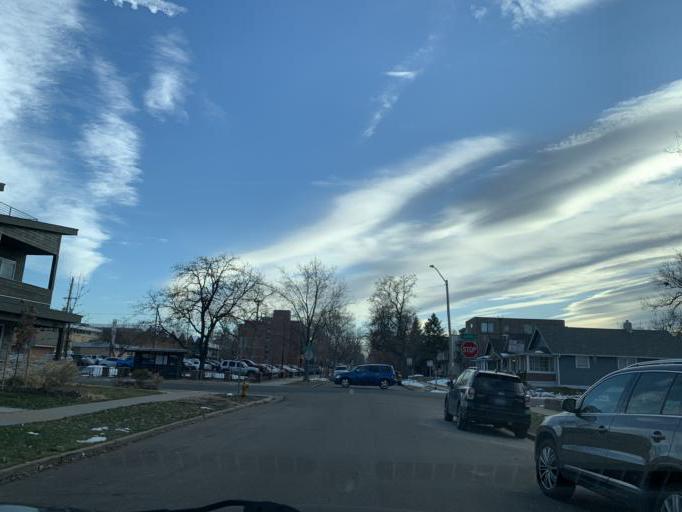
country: US
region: Colorado
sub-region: Jefferson County
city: Edgewater
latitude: 39.7769
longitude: -105.0463
